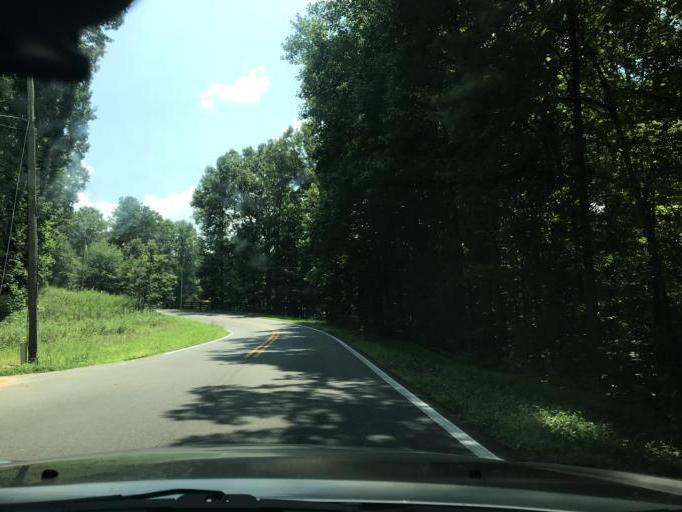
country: US
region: Georgia
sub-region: Forsyth County
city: Cumming
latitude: 34.2647
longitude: -84.2272
